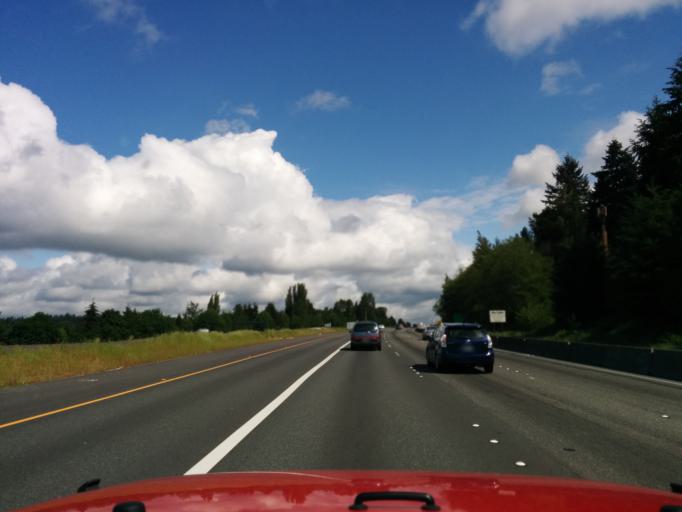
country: US
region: Washington
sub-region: King County
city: Kingsgate
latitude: 47.7248
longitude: -122.1892
